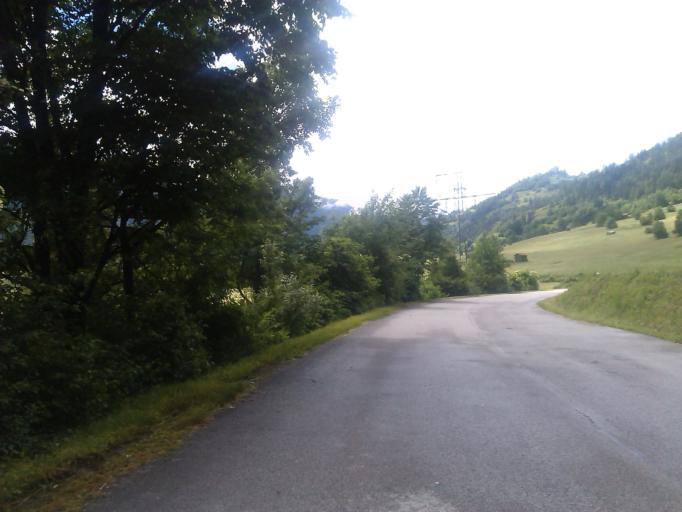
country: AT
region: Tyrol
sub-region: Politischer Bezirk Landeck
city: Prutz
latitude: 47.0951
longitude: 10.6629
